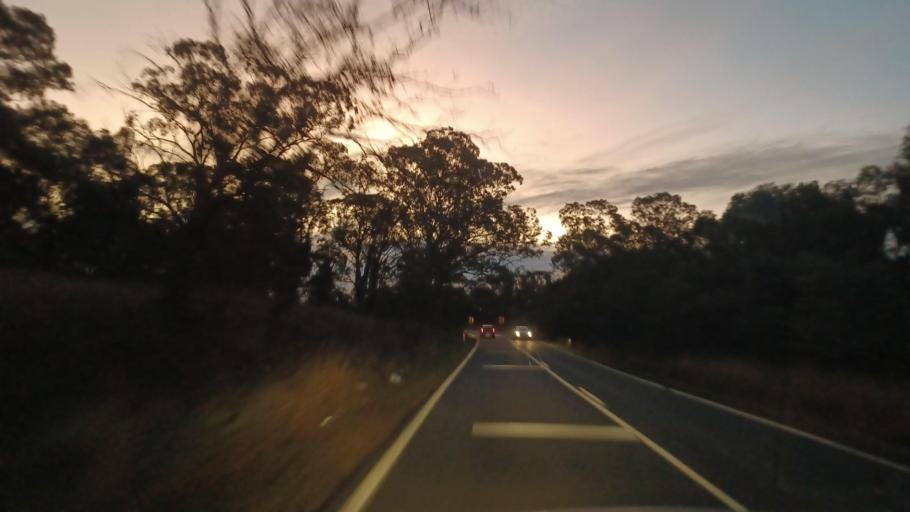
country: AU
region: Australian Capital Territory
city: Belconnen
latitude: -35.1897
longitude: 149.0585
